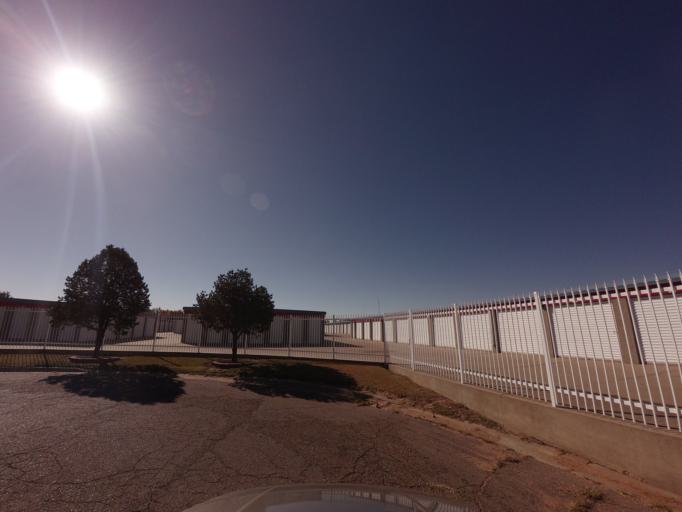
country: US
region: New Mexico
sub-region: Curry County
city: Clovis
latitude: 34.4330
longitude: -103.2011
